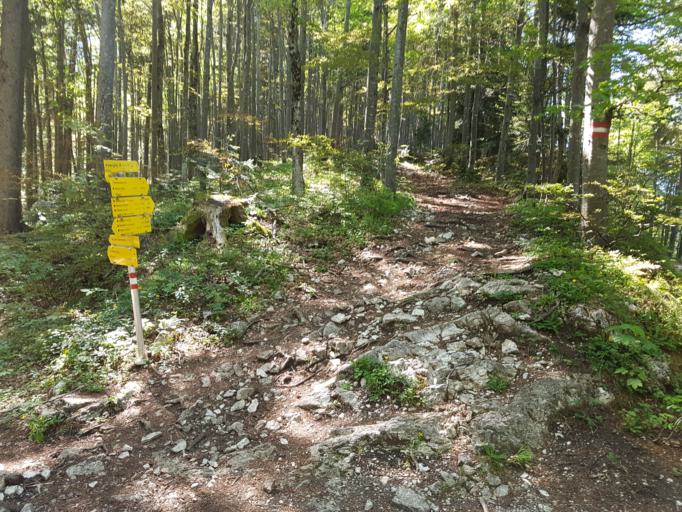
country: AT
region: Salzburg
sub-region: Politischer Bezirk Salzburg-Umgebung
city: Koppl
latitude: 47.7805
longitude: 13.1199
